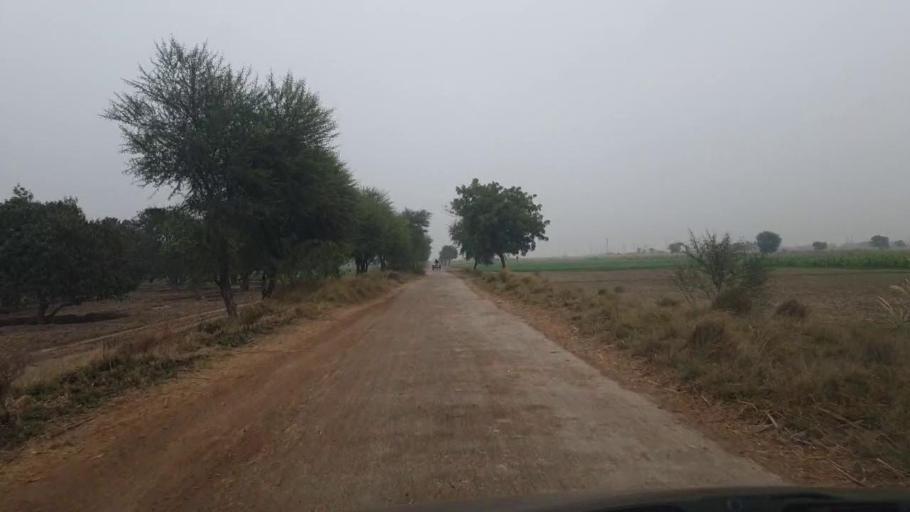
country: PK
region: Sindh
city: Tando Adam
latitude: 25.8028
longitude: 68.6813
